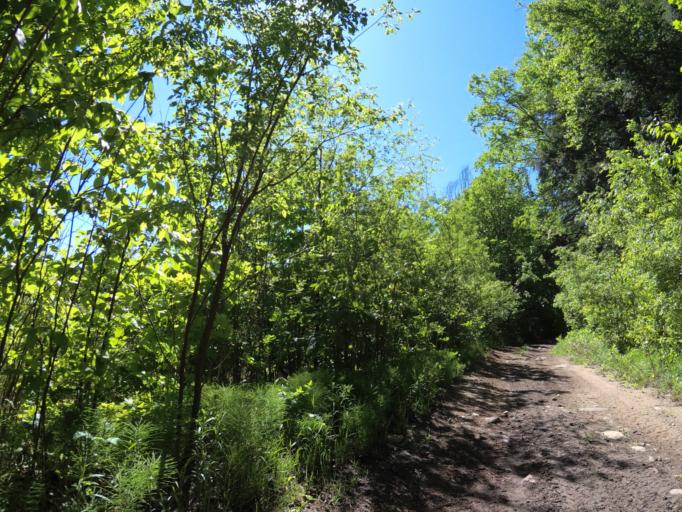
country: CA
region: Ontario
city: Renfrew
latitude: 45.0790
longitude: -77.0869
